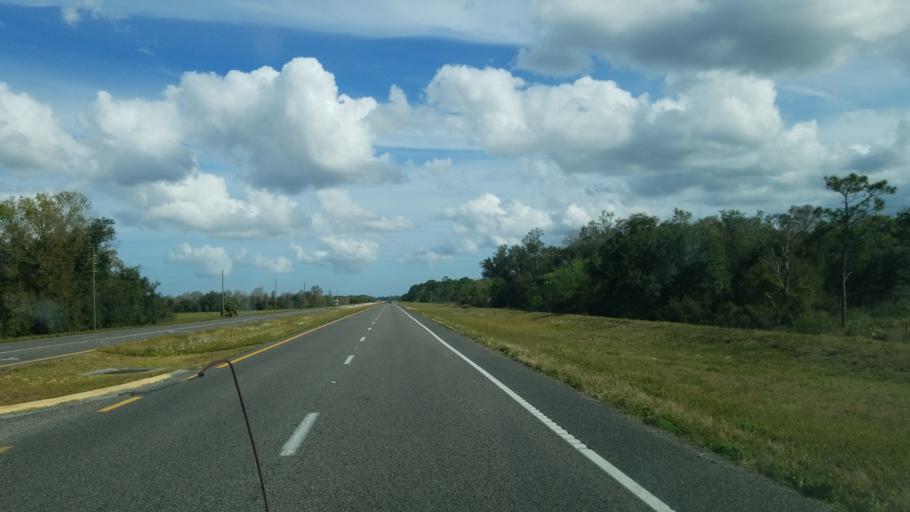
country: US
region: Florida
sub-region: Brevard County
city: June Park
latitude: 28.1214
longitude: -80.9527
